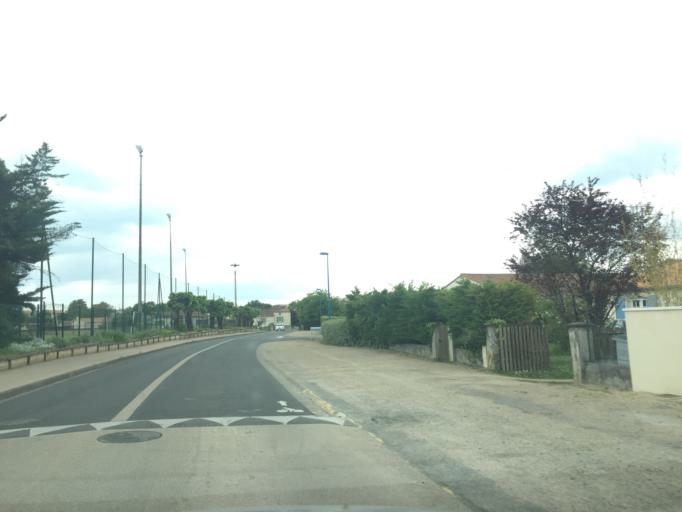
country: FR
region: Pays de la Loire
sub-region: Departement de la Vendee
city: Benet
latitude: 46.3717
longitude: -0.5863
